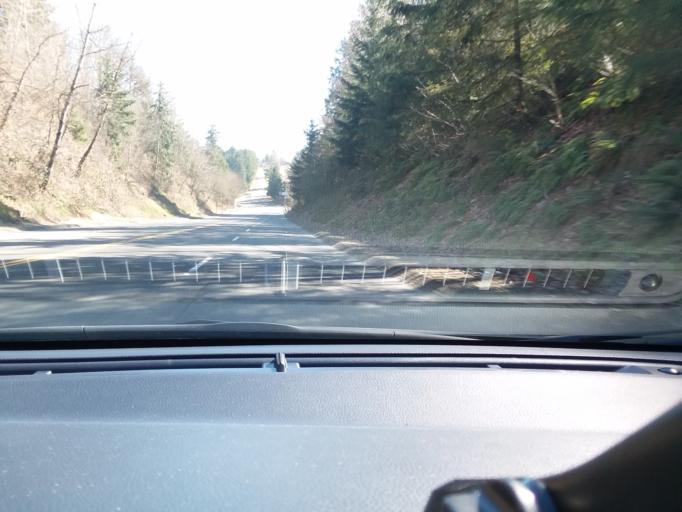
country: US
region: Washington
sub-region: Pierce County
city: Waller
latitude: 47.1917
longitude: -122.3536
